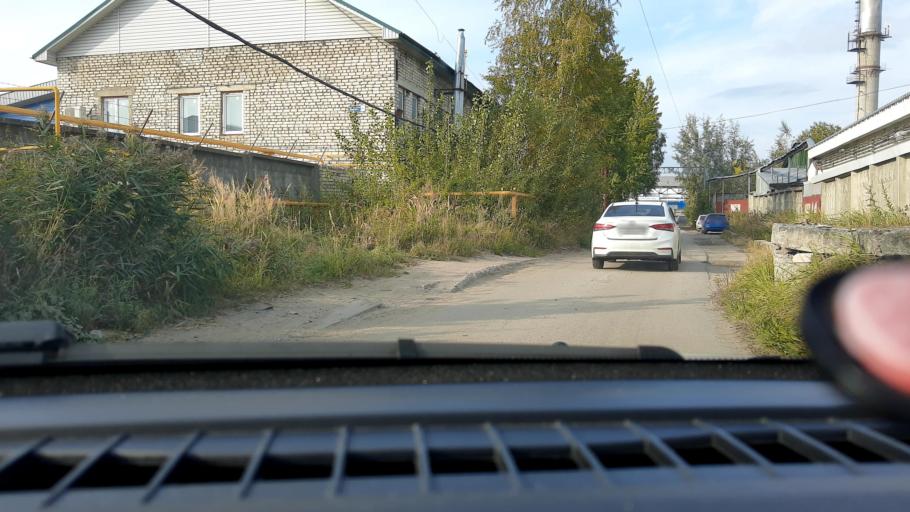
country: RU
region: Nizjnij Novgorod
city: Burevestnik
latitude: 56.1658
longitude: 43.9060
